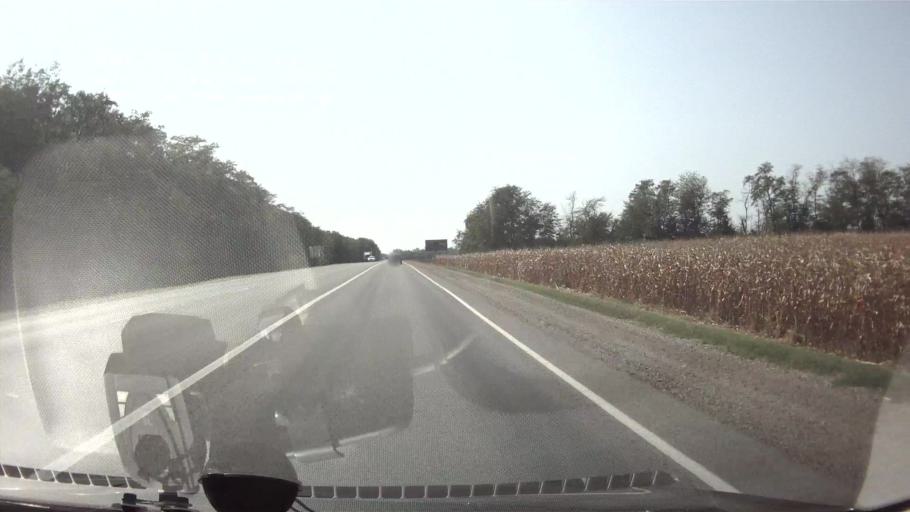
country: RU
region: Krasnodarskiy
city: Vasyurinskaya
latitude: 45.1509
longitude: 39.4418
